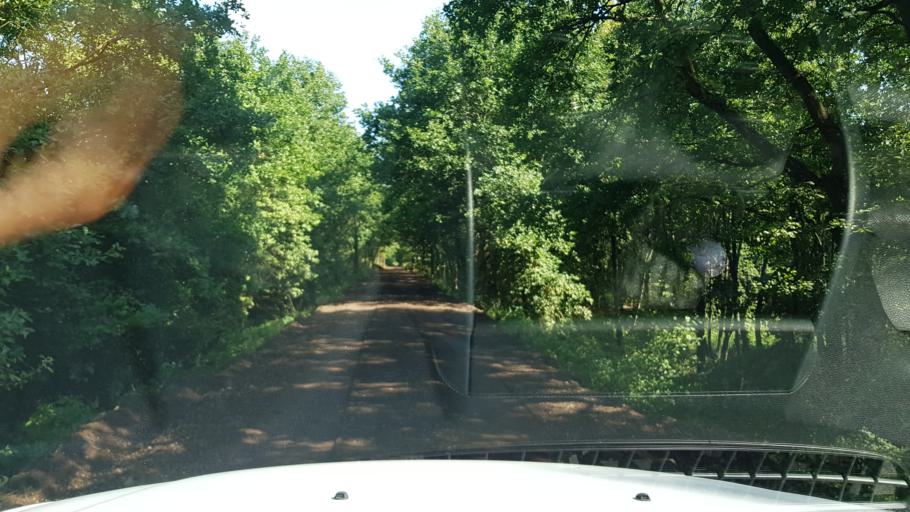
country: PL
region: West Pomeranian Voivodeship
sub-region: Powiat choszczenski
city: Pelczyce
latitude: 53.0647
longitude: 15.3059
